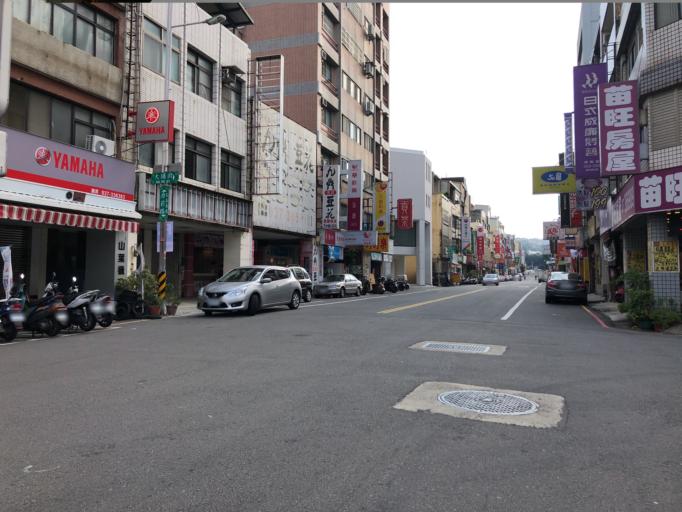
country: TW
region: Taiwan
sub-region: Miaoli
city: Miaoli
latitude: 24.5613
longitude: 120.8191
